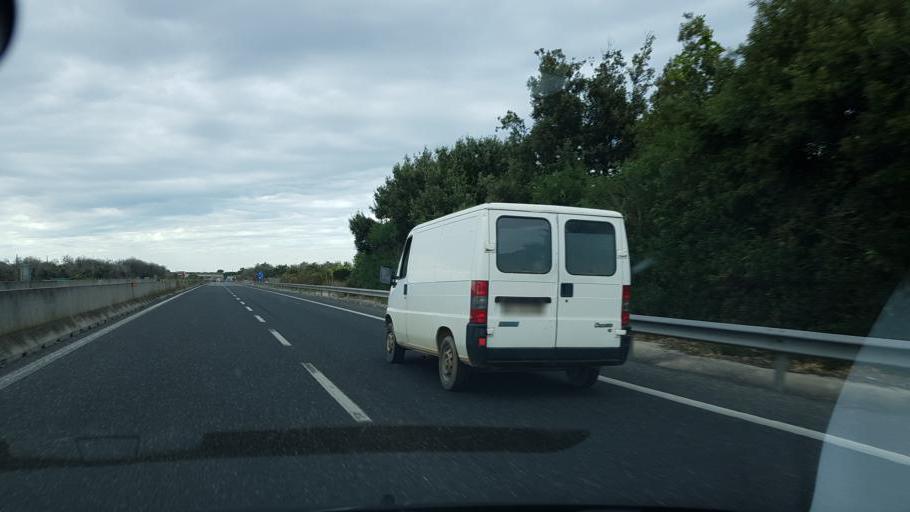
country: IT
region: Apulia
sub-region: Provincia di Brindisi
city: Torchiarolo
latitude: 40.4794
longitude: 18.0454
